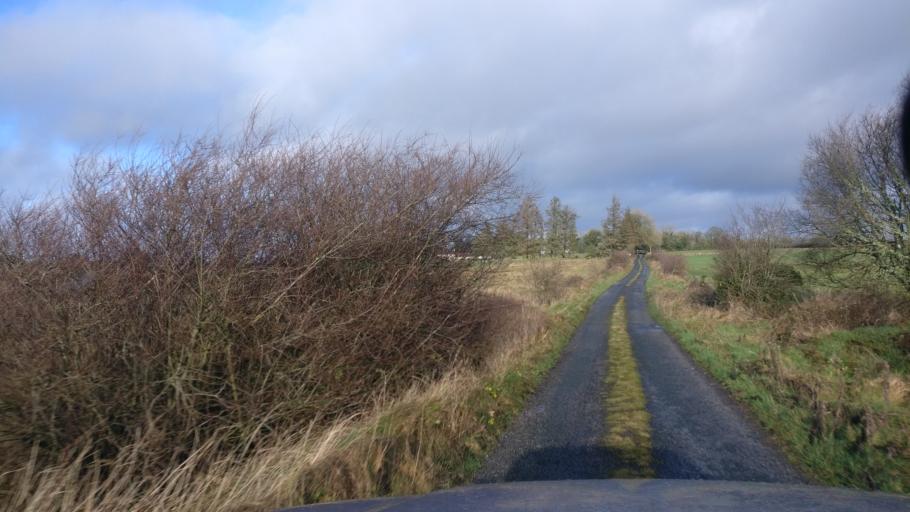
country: IE
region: Connaught
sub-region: County Galway
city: Loughrea
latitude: 53.2391
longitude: -8.5332
